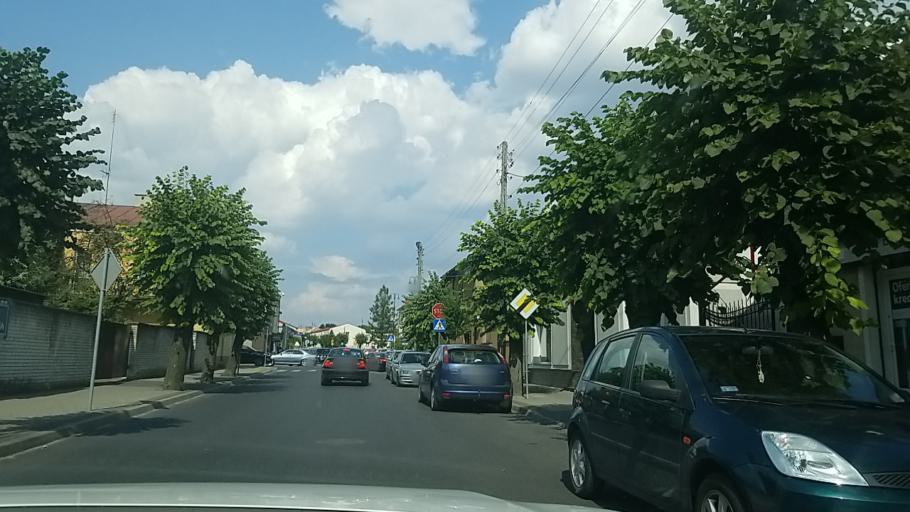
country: PL
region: Lublin Voivodeship
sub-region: Powiat janowski
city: Janow Lubelski
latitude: 50.7042
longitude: 22.4137
